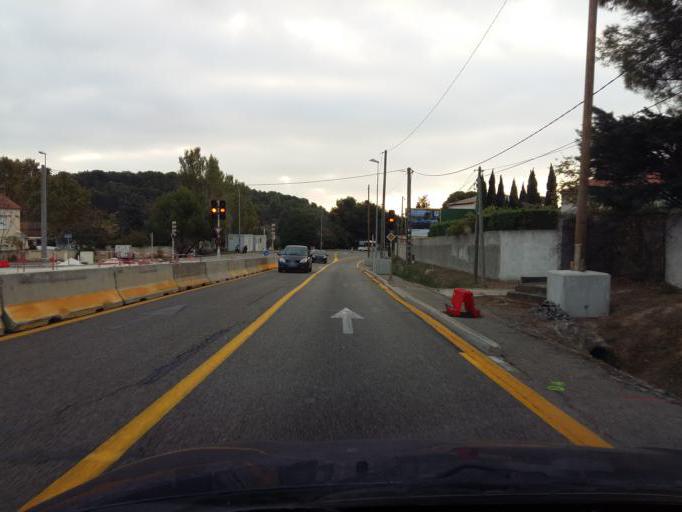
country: FR
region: Provence-Alpes-Cote d'Azur
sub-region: Departement des Bouches-du-Rhone
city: Martigues
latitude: 43.4273
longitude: 5.0506
